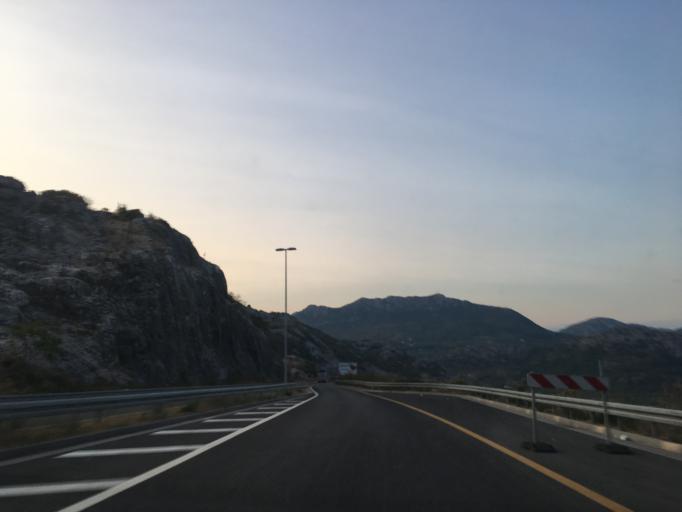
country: ME
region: Bar
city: Sutomore
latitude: 42.2040
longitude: 19.0506
